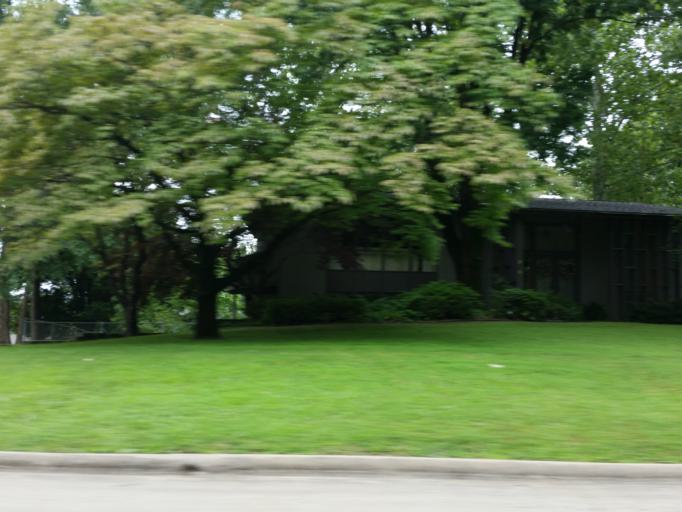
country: US
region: Missouri
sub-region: Cape Girardeau County
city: Cape Girardeau
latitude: 37.3349
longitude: -89.5494
